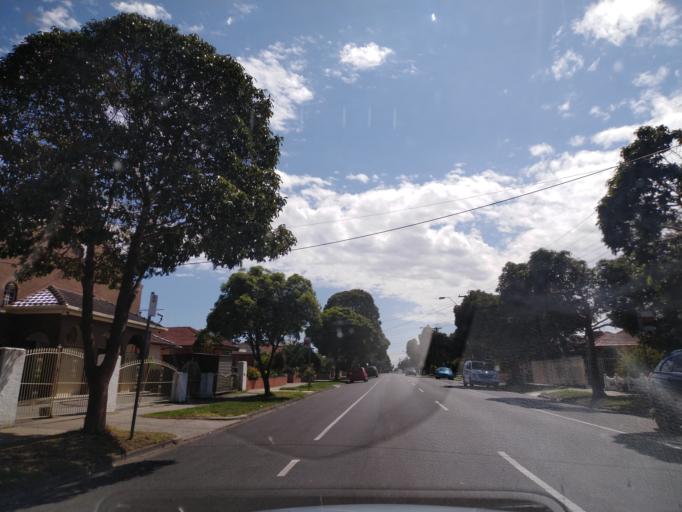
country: AU
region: Victoria
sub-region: Hobsons Bay
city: Altona North
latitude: -37.8374
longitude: 144.8554
